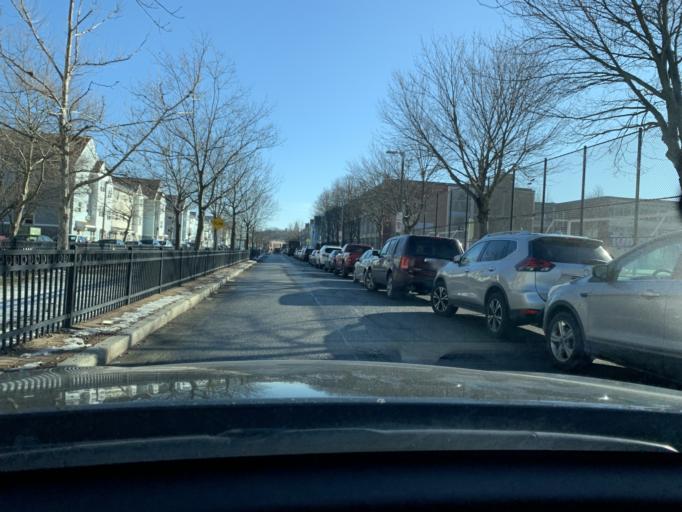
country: US
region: Massachusetts
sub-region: Norfolk County
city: Brookline
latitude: 42.3338
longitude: -71.0991
